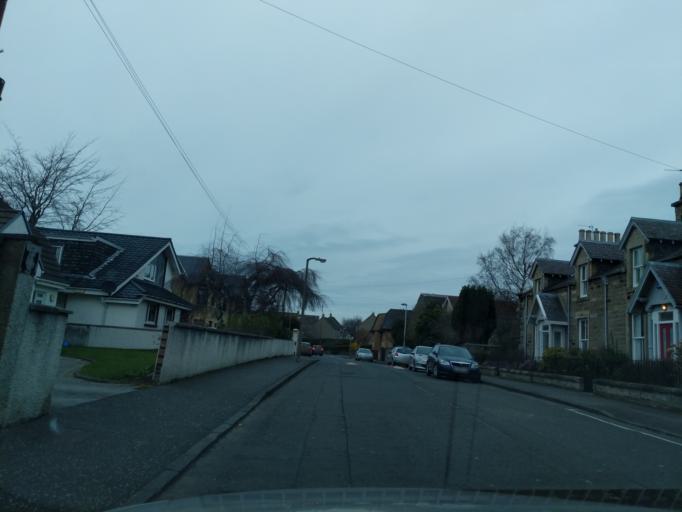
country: GB
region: Scotland
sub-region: Edinburgh
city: Colinton
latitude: 55.9391
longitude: -3.2867
